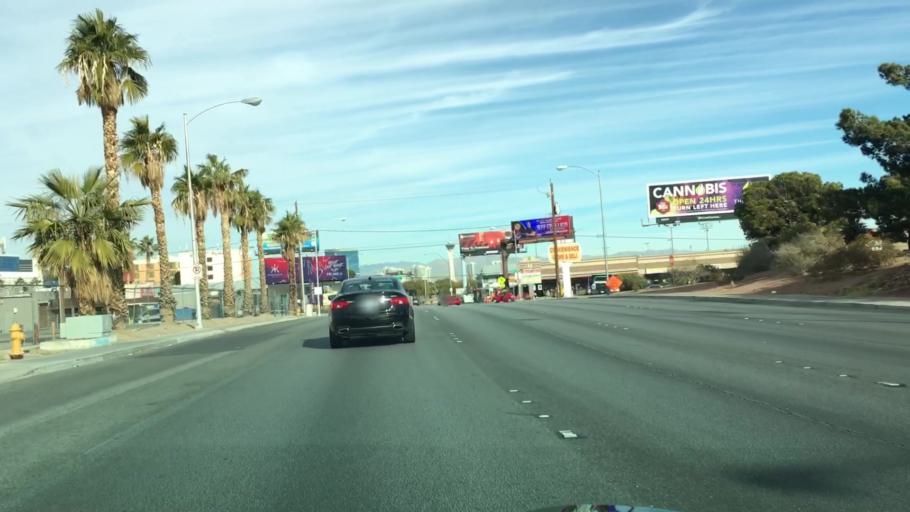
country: US
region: Nevada
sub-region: Clark County
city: Paradise
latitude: 36.1045
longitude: -115.1496
